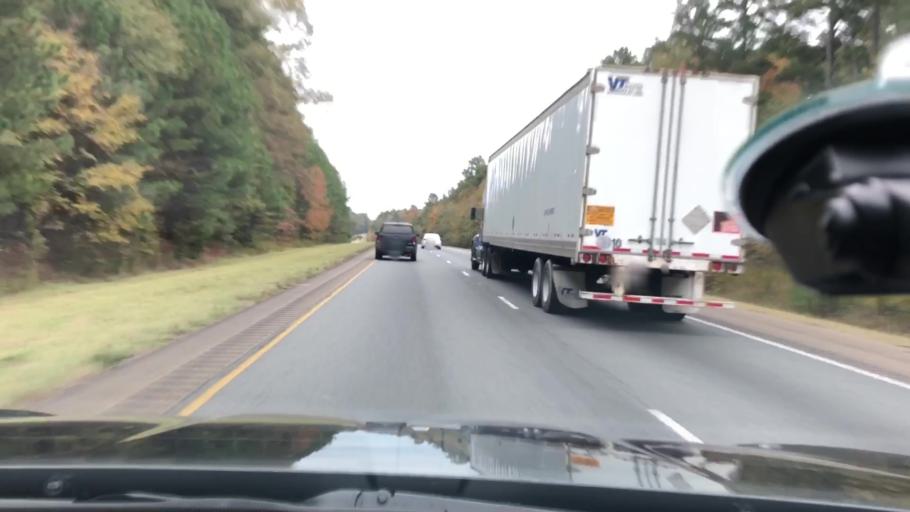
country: US
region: Arkansas
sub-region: Clark County
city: Gurdon
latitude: 33.9216
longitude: -93.2715
